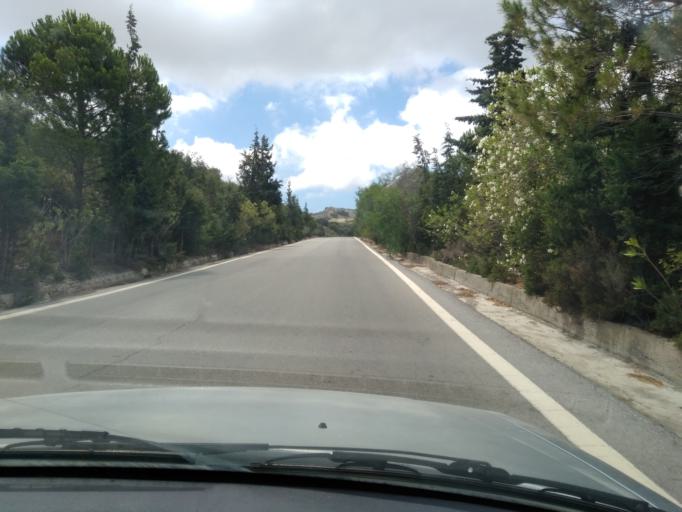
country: GR
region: Crete
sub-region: Nomos Lasithiou
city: Makry-Gialos
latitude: 35.0679
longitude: 26.0470
